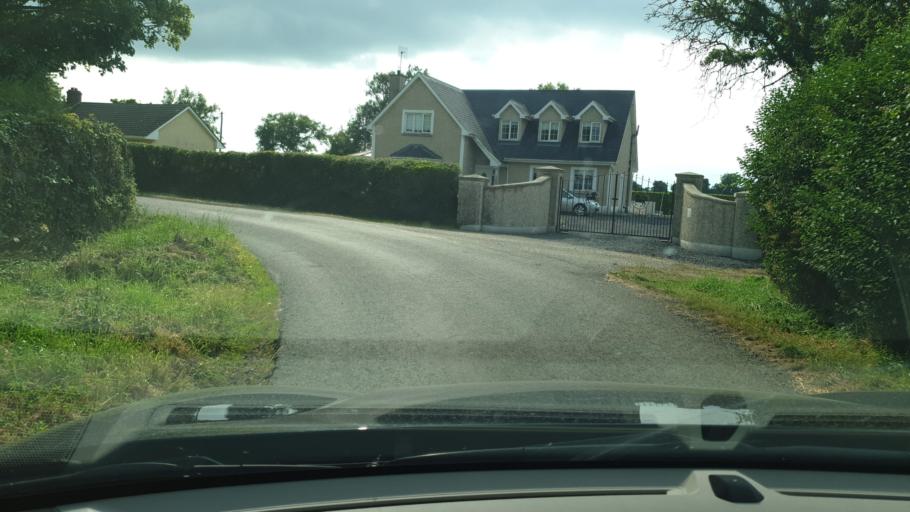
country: IE
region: Leinster
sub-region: An Mhi
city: Ratoath
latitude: 53.4736
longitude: -6.4500
